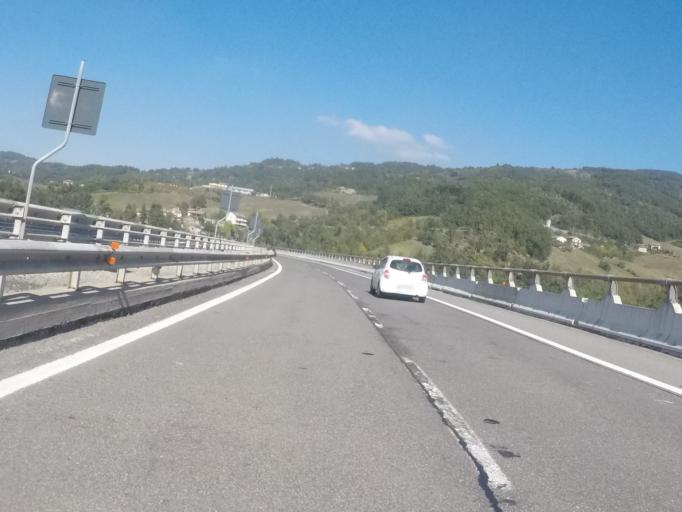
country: IT
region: Emilia-Romagna
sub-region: Provincia di Bologna
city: San Benedetto Val di Sambro
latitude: 44.1711
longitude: 11.2127
